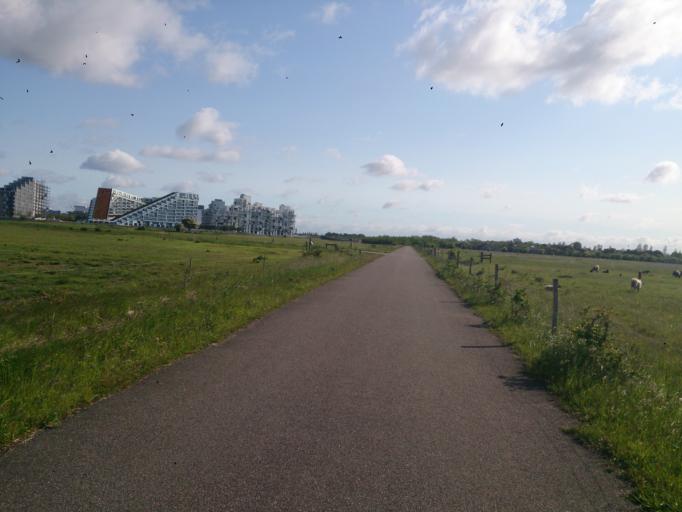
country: DK
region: Capital Region
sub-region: Tarnby Kommune
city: Tarnby
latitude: 55.6116
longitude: 12.5688
